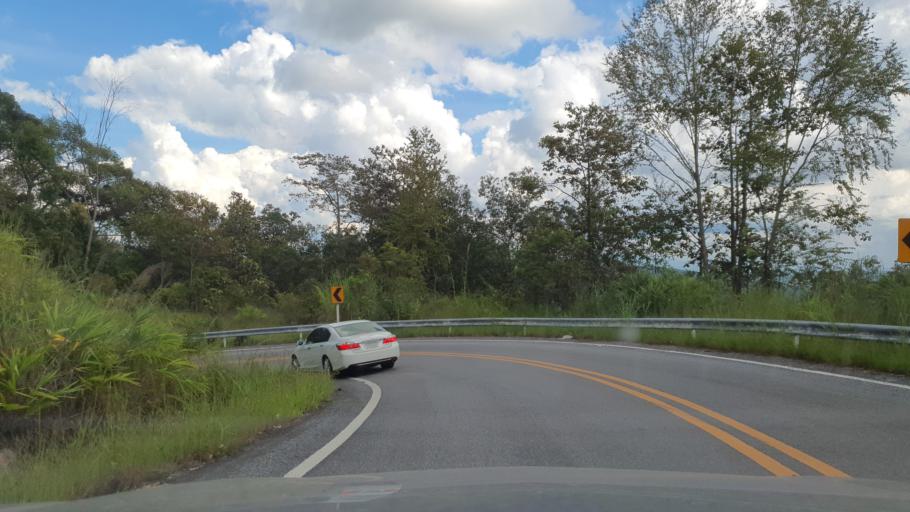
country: TH
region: Chiang Rai
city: Wiang Pa Pao
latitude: 19.3143
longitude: 99.3935
